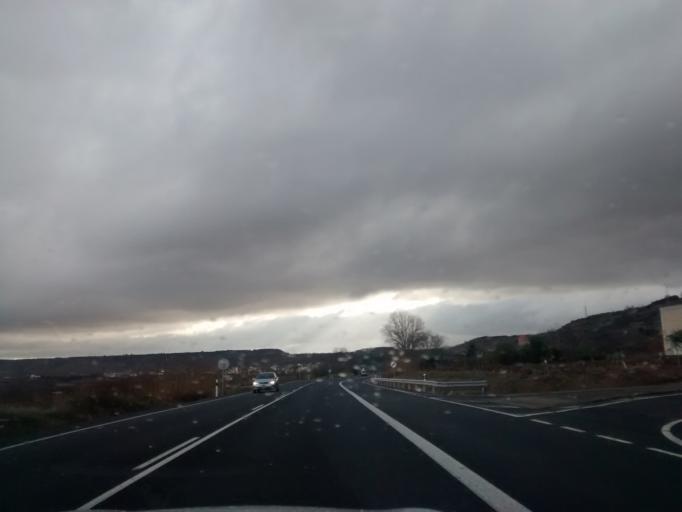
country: ES
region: La Rioja
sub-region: Provincia de La Rioja
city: Torremontalbo
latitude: 42.4908
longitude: -2.6639
